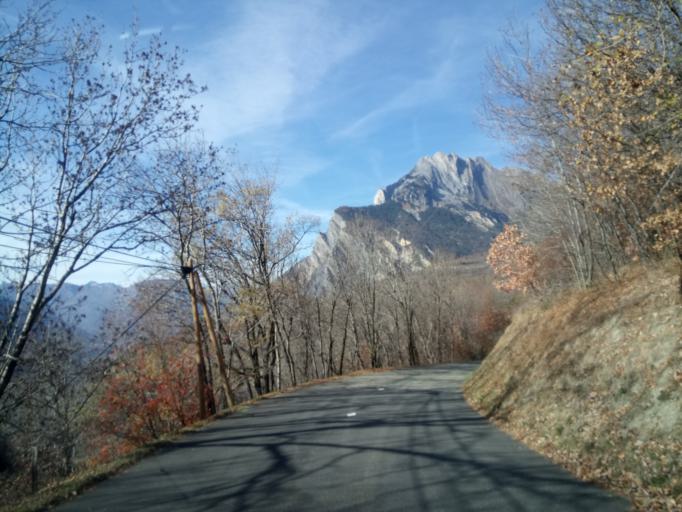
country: FR
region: Rhone-Alpes
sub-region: Departement de la Savoie
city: Saint-Michel-de-Maurienne
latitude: 45.2281
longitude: 6.4742
